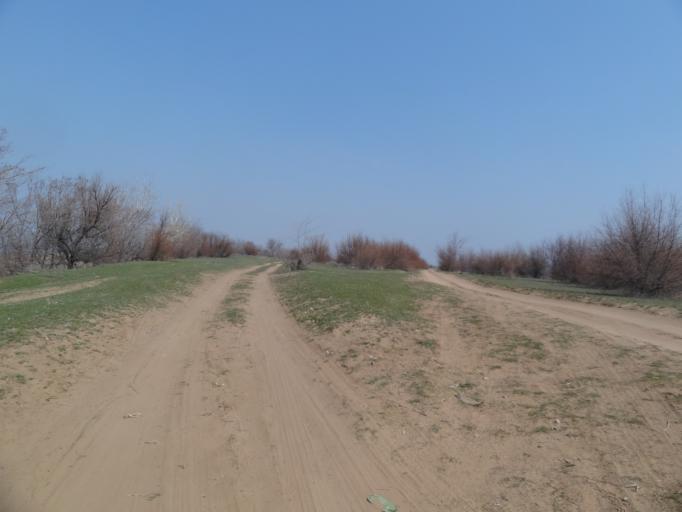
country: RU
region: Saratov
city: Privolzhskiy
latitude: 51.2703
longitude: 45.9296
